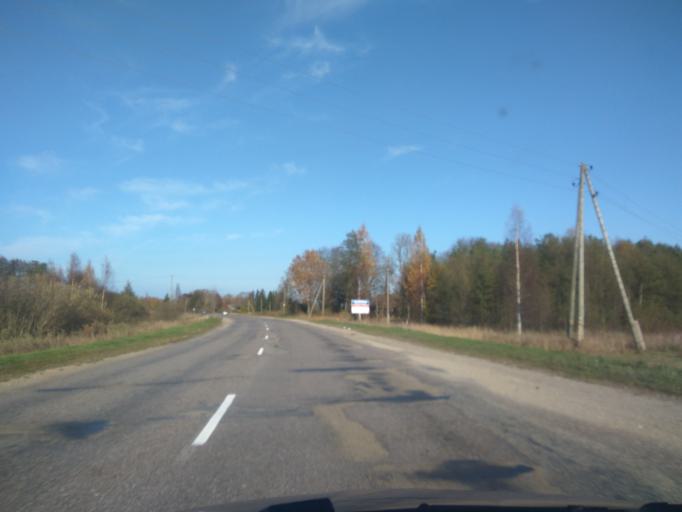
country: LV
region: Ventspils
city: Ventspils
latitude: 57.3420
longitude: 21.5689
